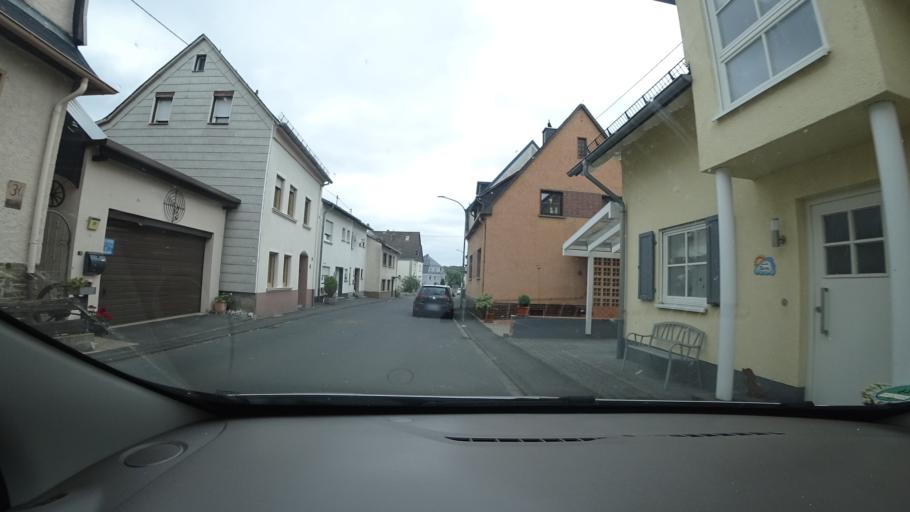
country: DE
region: Rheinland-Pfalz
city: Hohr-Grenzhausen
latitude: 50.4409
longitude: 7.6595
